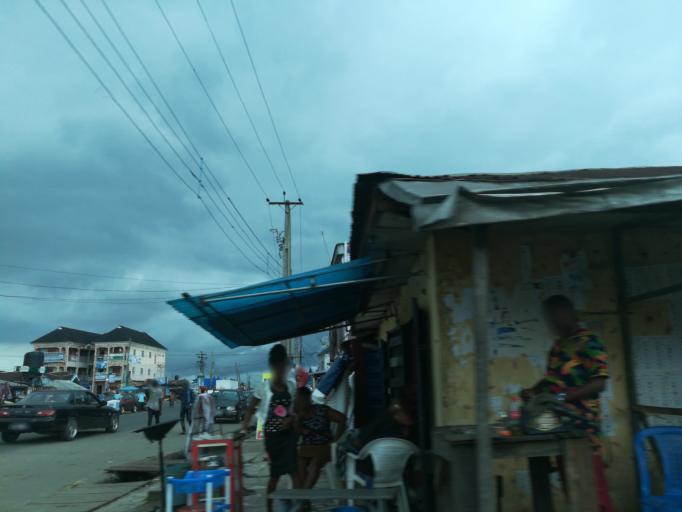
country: NG
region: Rivers
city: Port Harcourt
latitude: 4.7966
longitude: 6.9878
